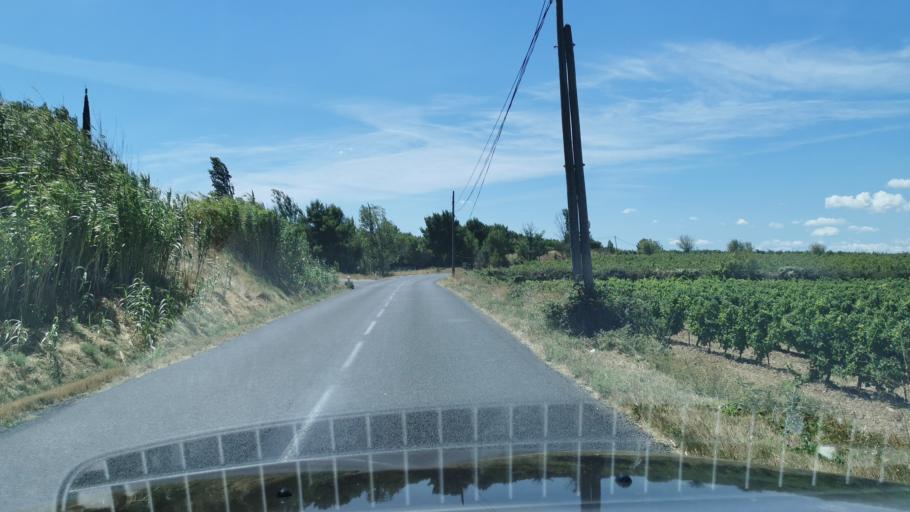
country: FR
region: Languedoc-Roussillon
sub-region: Departement de l'Aude
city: Vinassan
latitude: 43.1922
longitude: 3.0679
